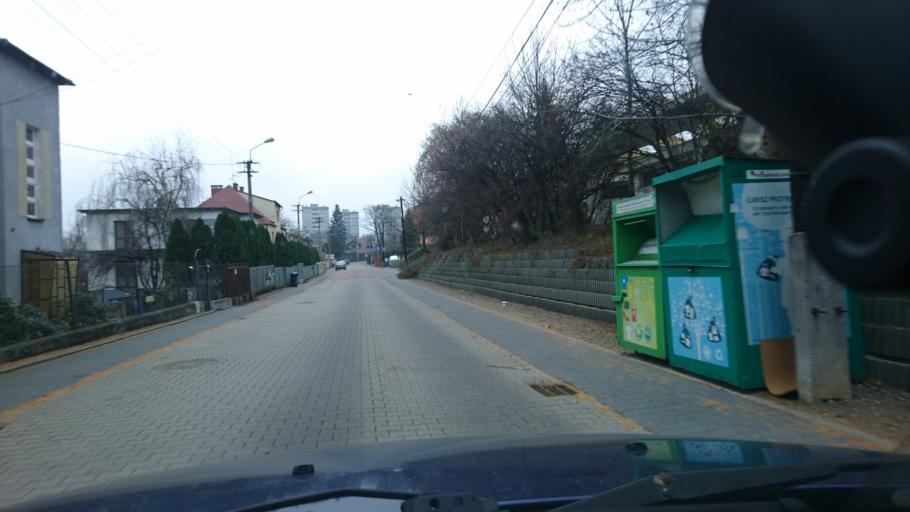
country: PL
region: Silesian Voivodeship
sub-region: Bielsko-Biala
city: Bielsko-Biala
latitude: 49.8123
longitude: 19.0170
